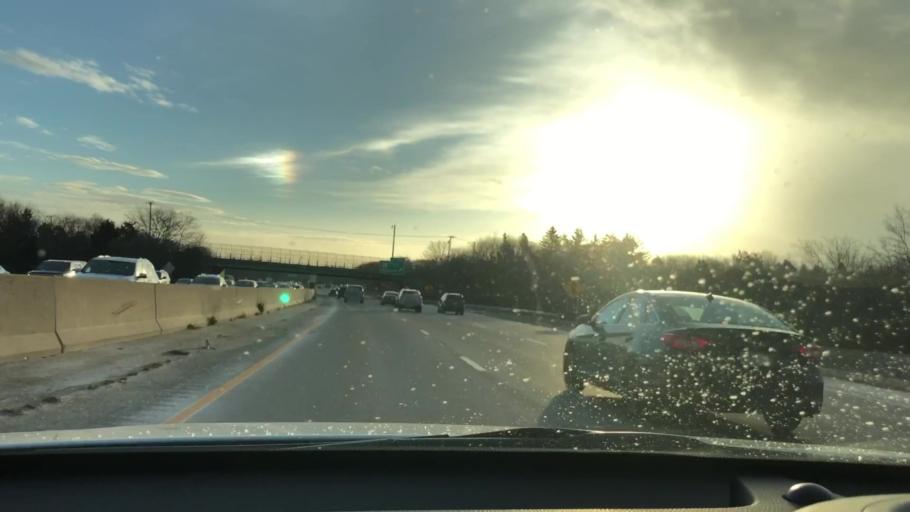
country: US
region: Massachusetts
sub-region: Norfolk County
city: Weymouth
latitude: 42.1951
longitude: -70.9578
